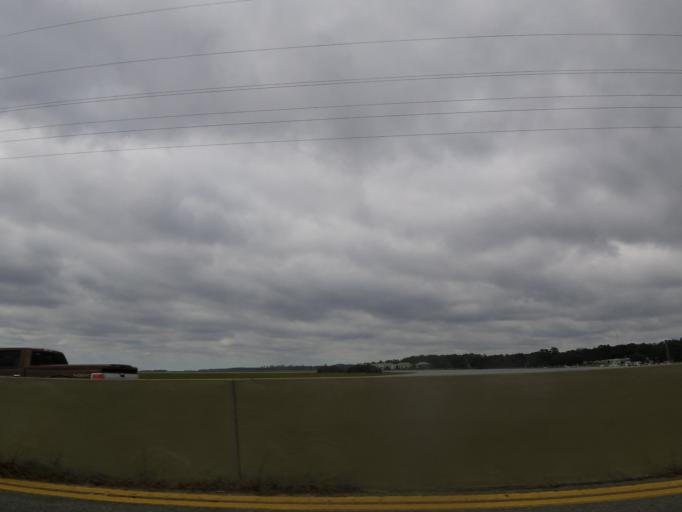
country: US
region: Georgia
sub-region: Glynn County
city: Saint Simon Mills
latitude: 31.1680
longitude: -81.4138
